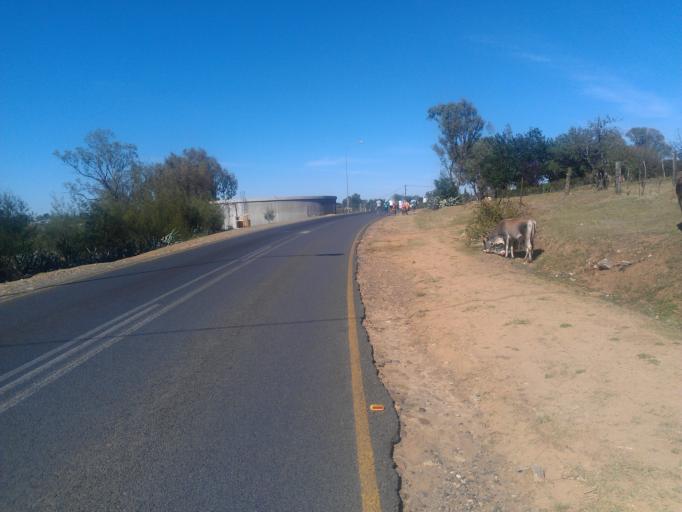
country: LS
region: Berea
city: Teyateyaneng
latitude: -29.1406
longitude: 27.7567
